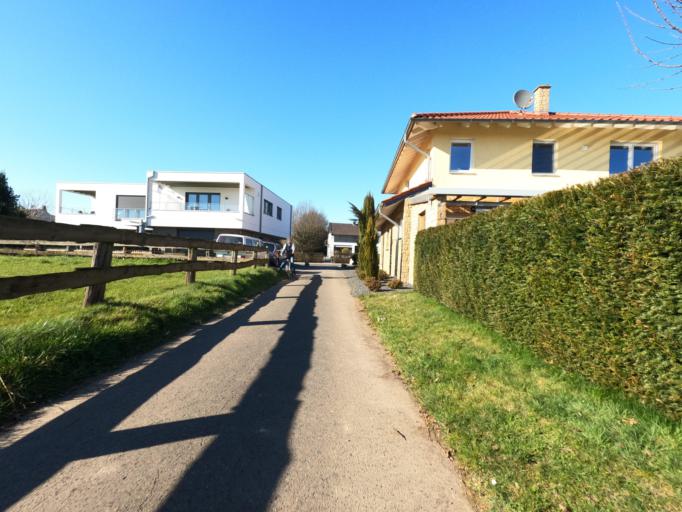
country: DE
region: North Rhine-Westphalia
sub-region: Regierungsbezirk Koln
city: Linnich
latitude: 50.9998
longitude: 6.3233
